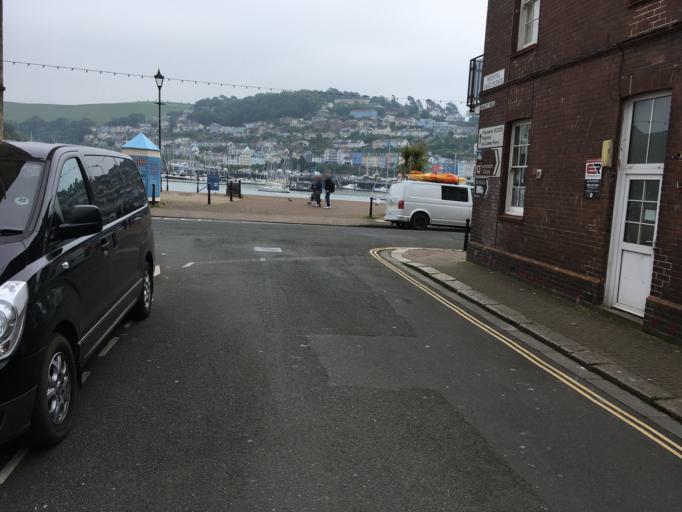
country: GB
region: England
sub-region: Devon
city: Dartmouth
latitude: 50.3504
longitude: -3.5777
